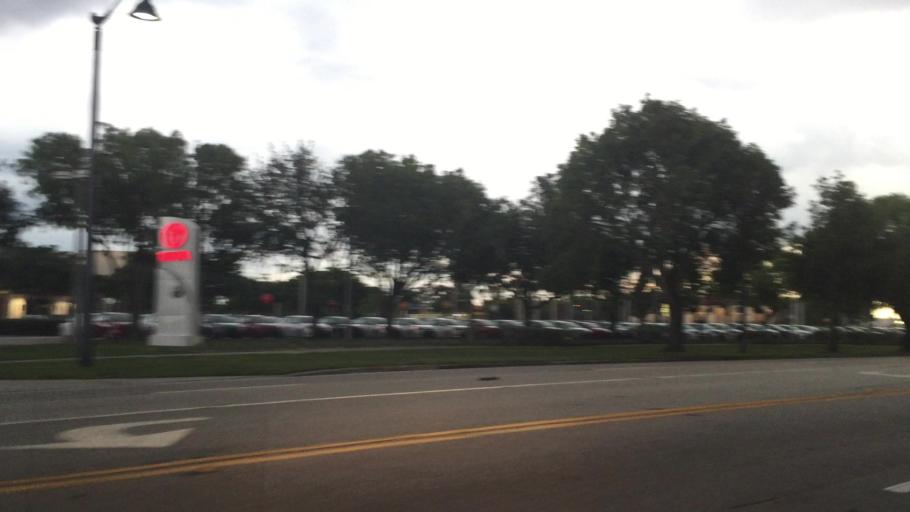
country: US
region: Florida
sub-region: Lee County
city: Pine Manor
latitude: 26.5988
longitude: -81.8620
